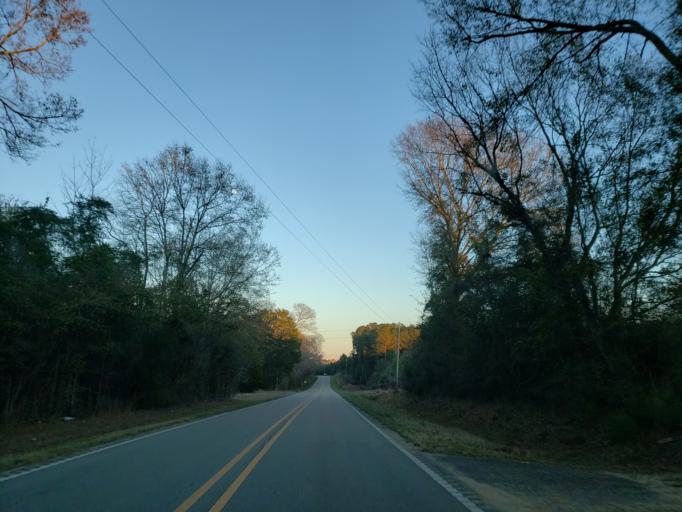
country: US
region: Mississippi
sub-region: Covington County
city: Collins
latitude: 31.5653
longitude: -89.4349
